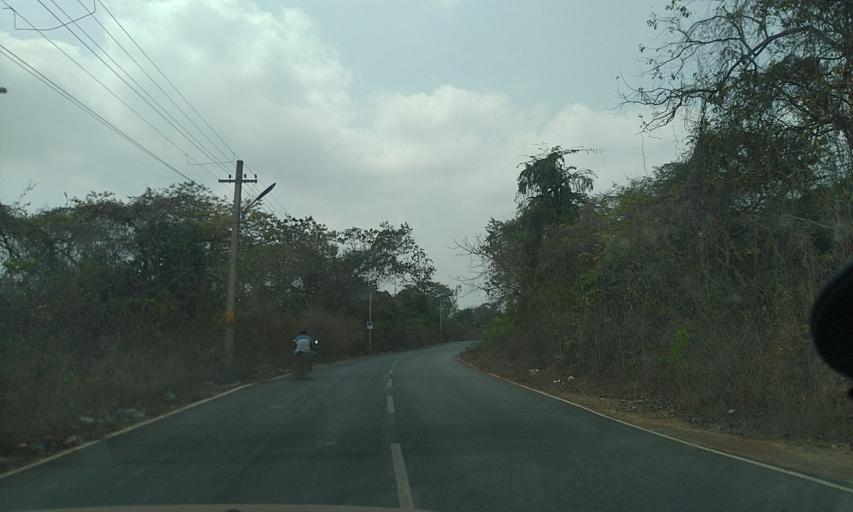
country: IN
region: Goa
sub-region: North Goa
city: Goa Velha
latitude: 15.4894
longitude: 73.9111
